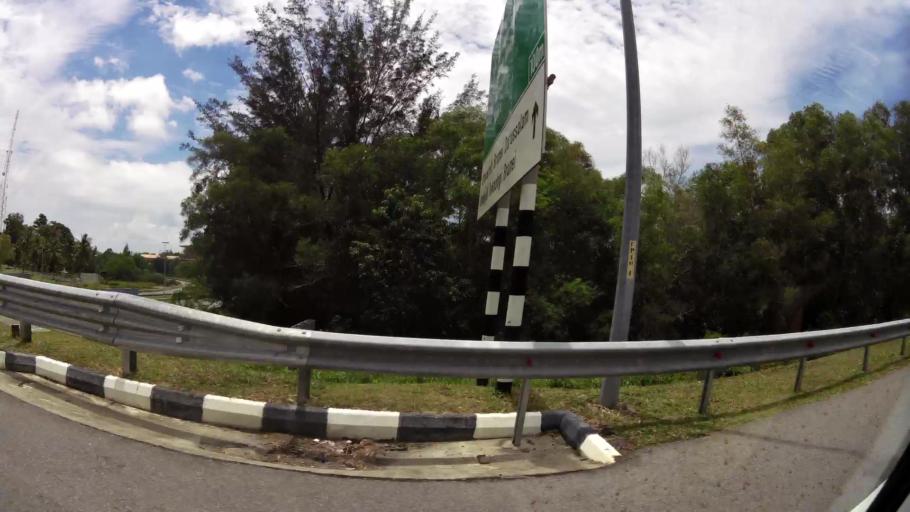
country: BN
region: Brunei and Muara
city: Bandar Seri Begawan
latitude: 4.9687
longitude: 114.8858
